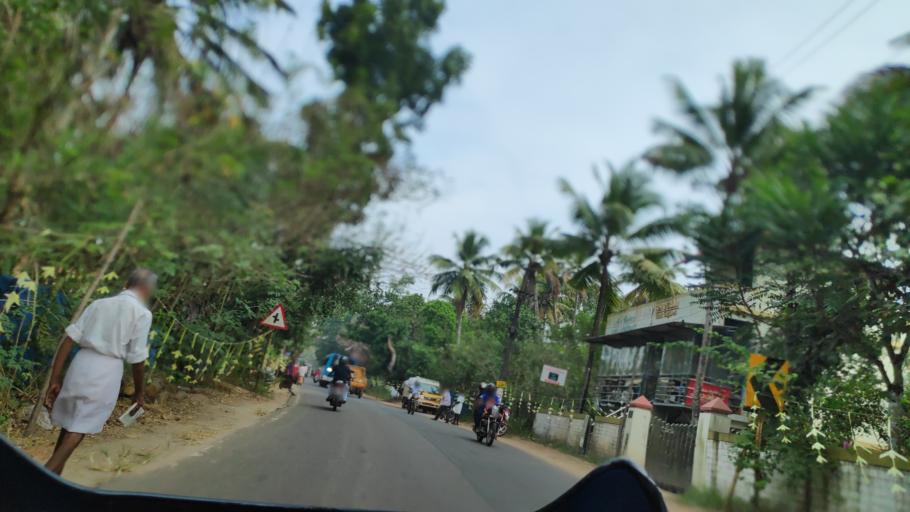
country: IN
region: Kerala
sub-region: Alappuzha
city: Vayalar
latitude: 9.7128
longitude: 76.3589
